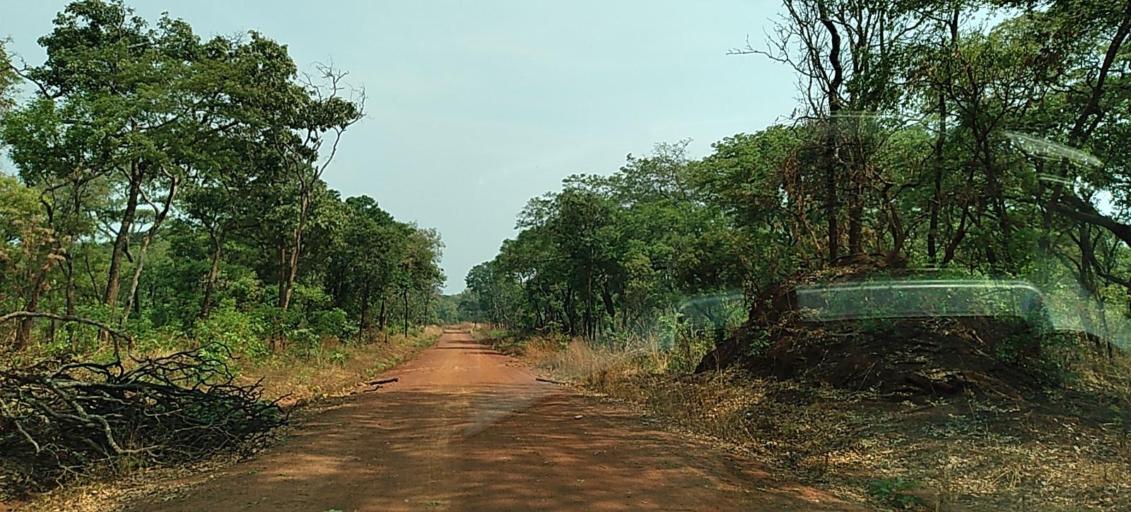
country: ZM
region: North-Western
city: Kansanshi
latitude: -11.9936
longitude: 26.8370
